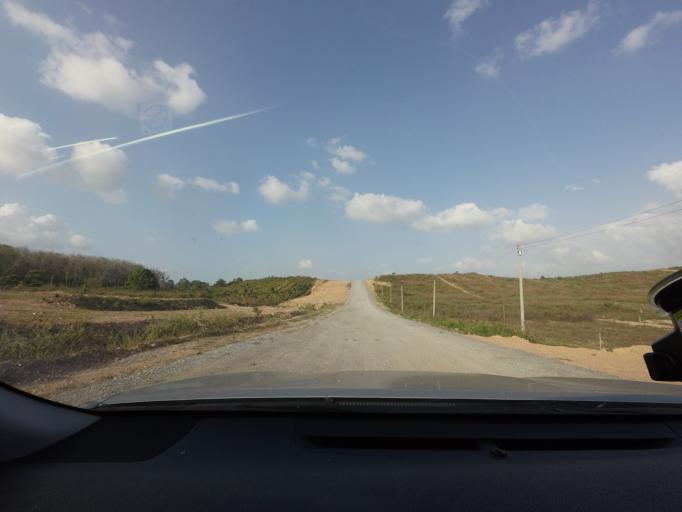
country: TH
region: Pattani
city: Mae Lan
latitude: 6.6104
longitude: 101.2547
